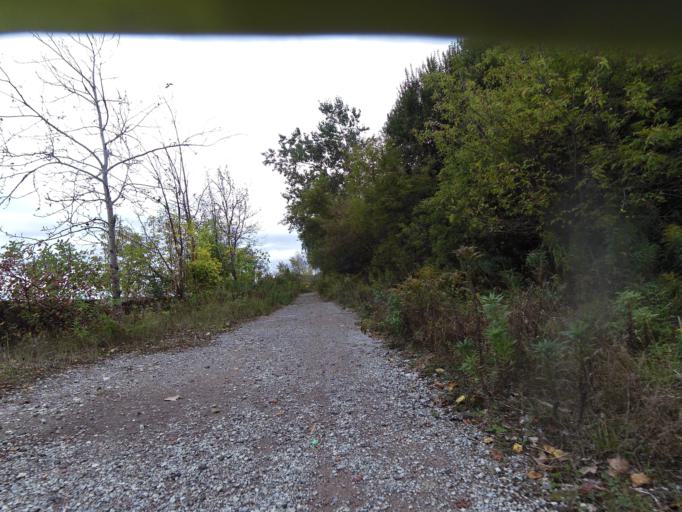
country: CA
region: Ontario
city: Scarborough
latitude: 43.7500
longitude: -79.1826
